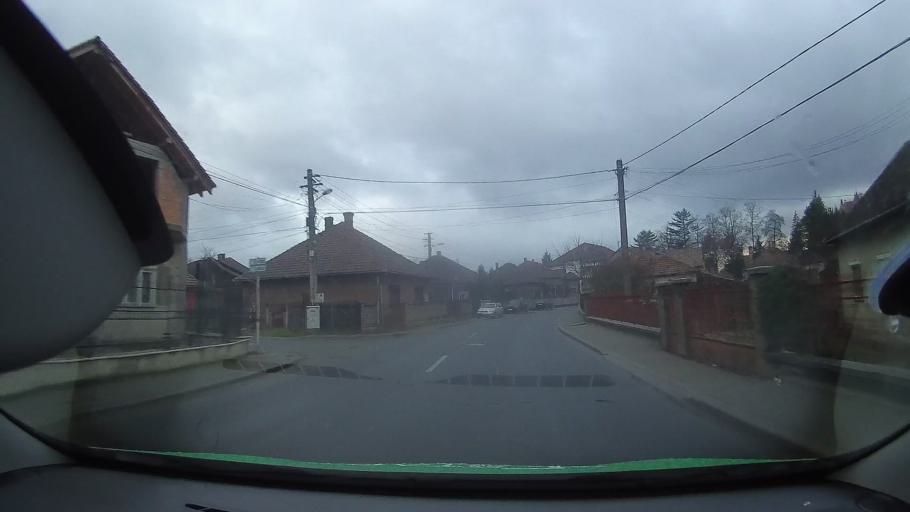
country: RO
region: Hunedoara
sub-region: Municipiul Brad
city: Brad
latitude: 46.1290
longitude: 22.7848
